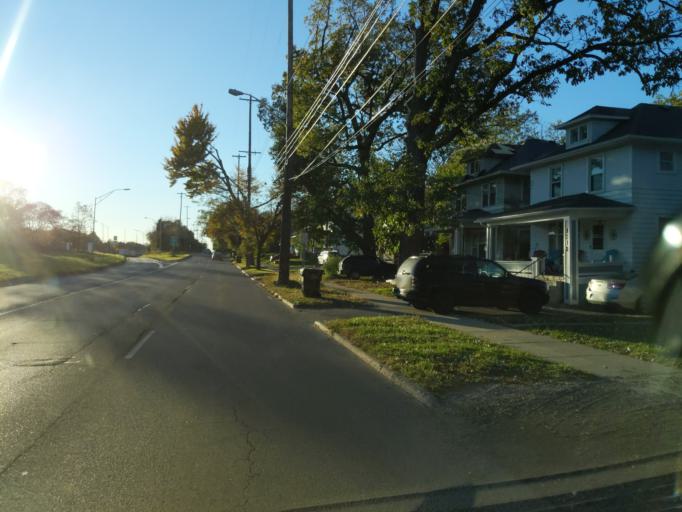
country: US
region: Michigan
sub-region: Ingham County
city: Lansing
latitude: 42.7265
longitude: -84.5704
